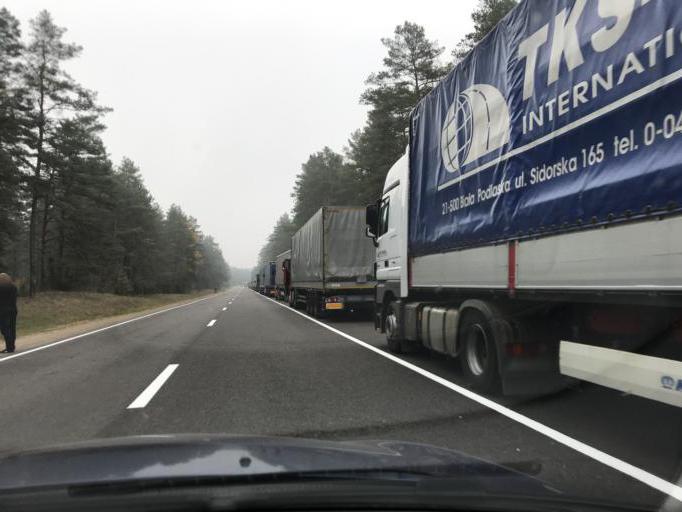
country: LT
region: Alytaus apskritis
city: Druskininkai
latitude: 53.9255
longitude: 23.9331
